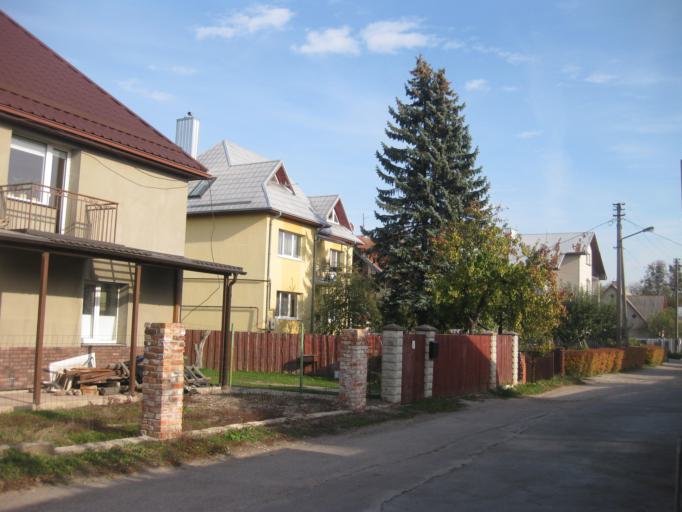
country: LT
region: Kauno apskritis
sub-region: Kaunas
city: Aleksotas
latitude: 54.8888
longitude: 23.8907
